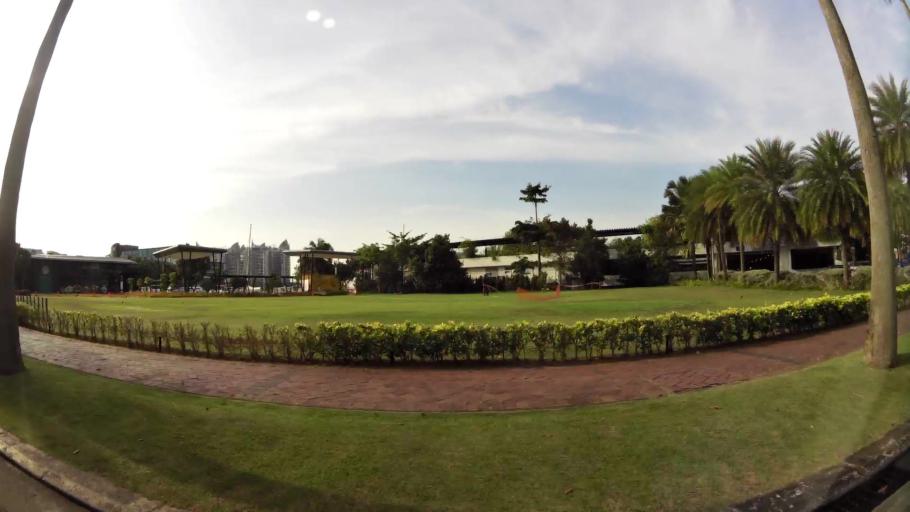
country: SG
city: Singapore
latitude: 1.2489
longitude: 103.8408
